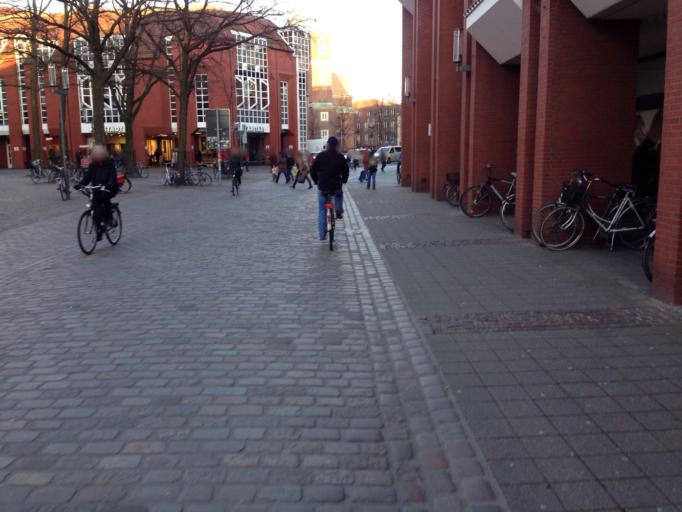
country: DE
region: North Rhine-Westphalia
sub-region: Regierungsbezirk Munster
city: Muenster
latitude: 51.9610
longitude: 7.6289
